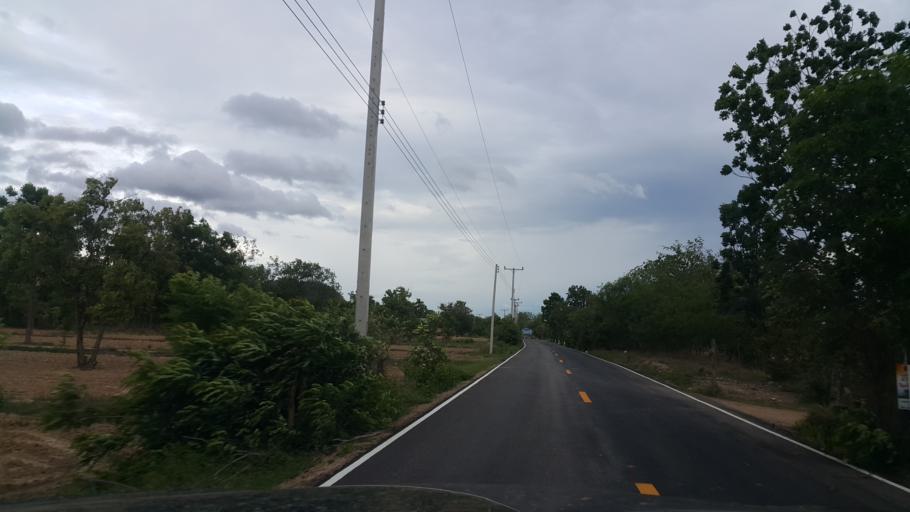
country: TH
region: Sukhothai
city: Thung Saliam
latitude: 17.1721
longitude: 99.4869
